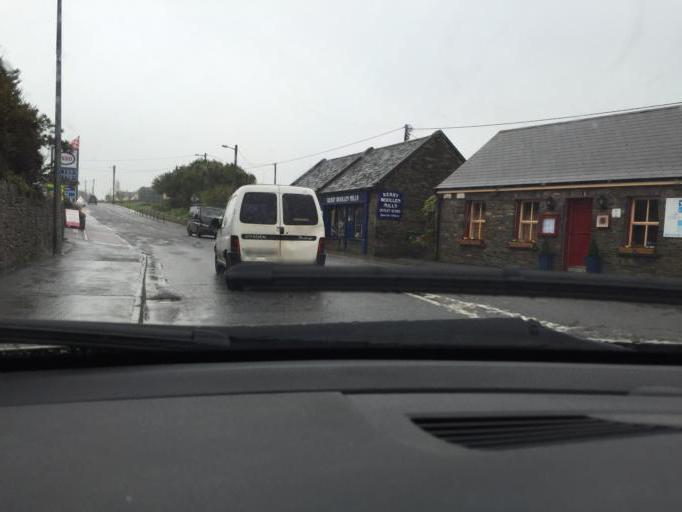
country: IE
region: Munster
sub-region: Ciarrai
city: Dingle
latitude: 52.1387
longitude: -10.2705
